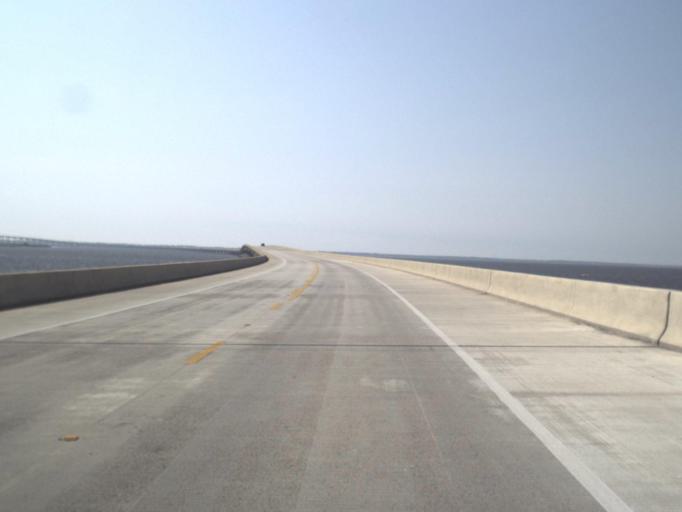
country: US
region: Florida
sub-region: Franklin County
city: Eastpoint
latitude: 29.7138
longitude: -84.8909
